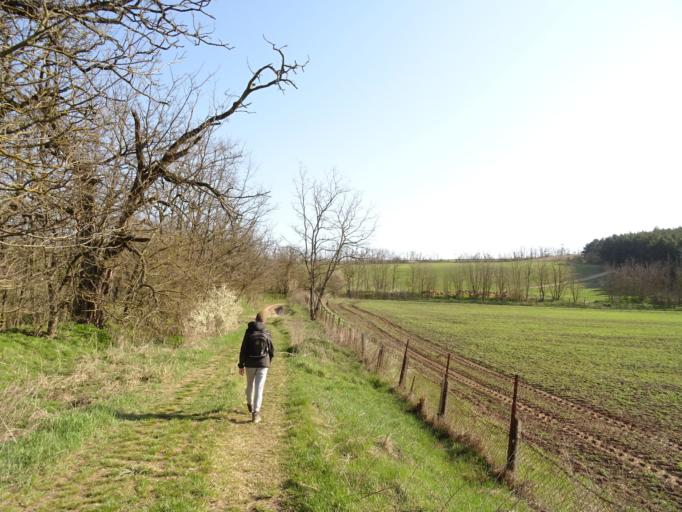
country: HU
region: Pest
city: Godollo
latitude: 47.6246
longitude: 19.3844
